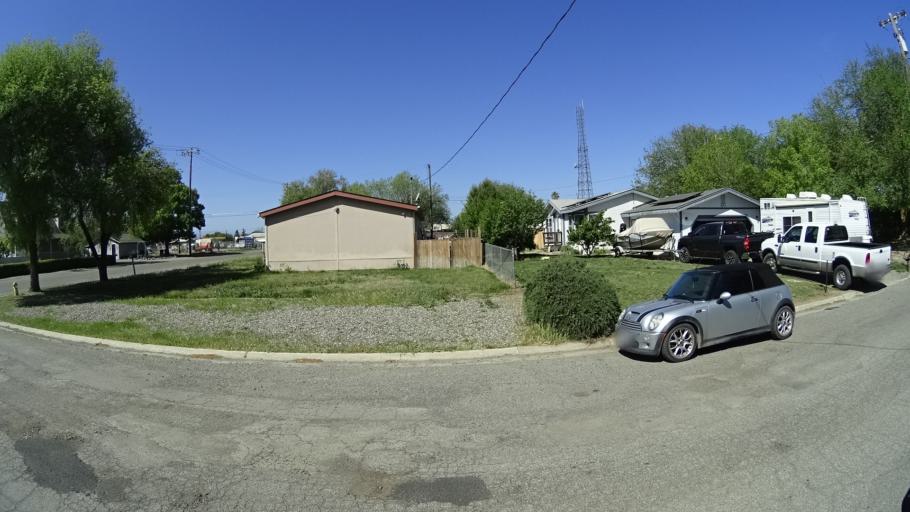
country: US
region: California
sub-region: Glenn County
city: Willows
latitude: 39.5293
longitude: -122.1909
